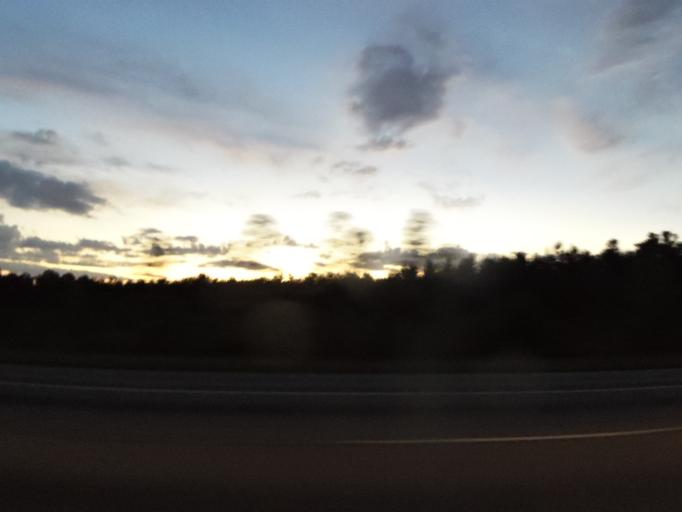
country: US
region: Georgia
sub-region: Liberty County
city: Midway
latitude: 31.6169
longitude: -81.4134
